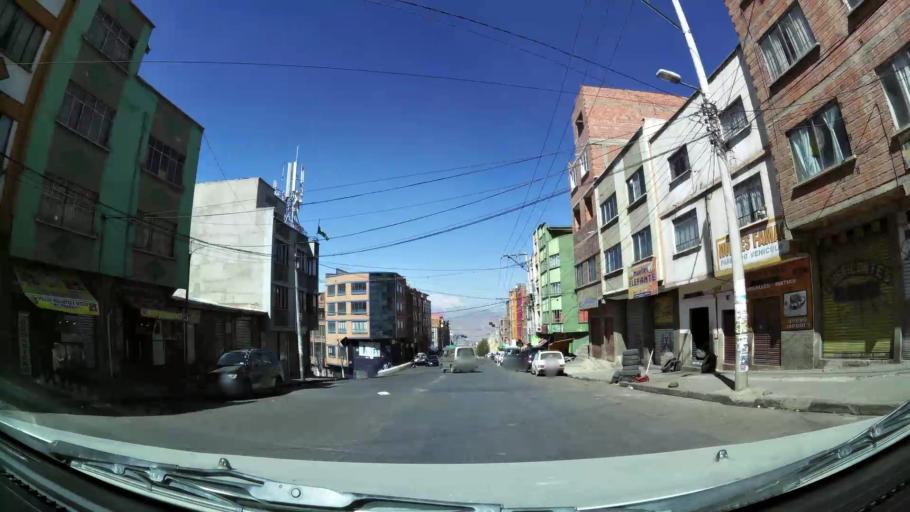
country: BO
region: La Paz
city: La Paz
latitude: -16.4966
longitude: -68.1571
